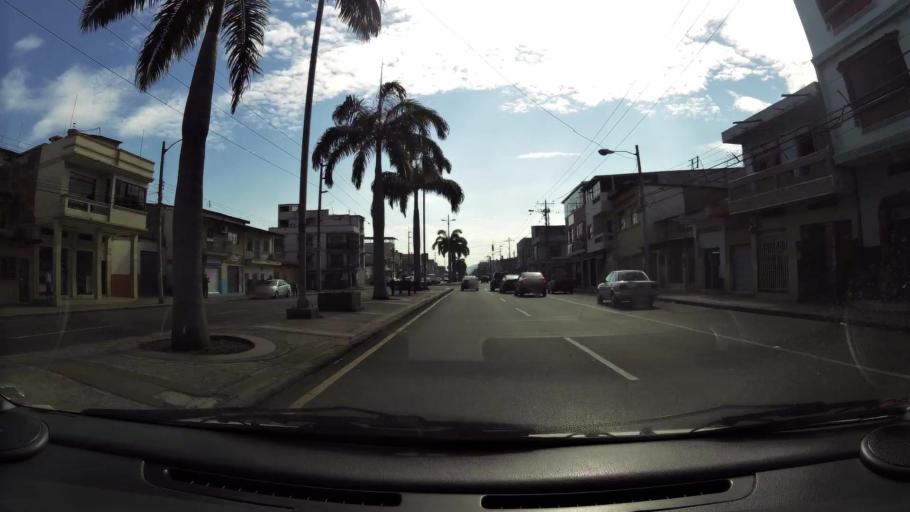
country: EC
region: Guayas
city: Guayaquil
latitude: -2.2005
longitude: -79.9209
